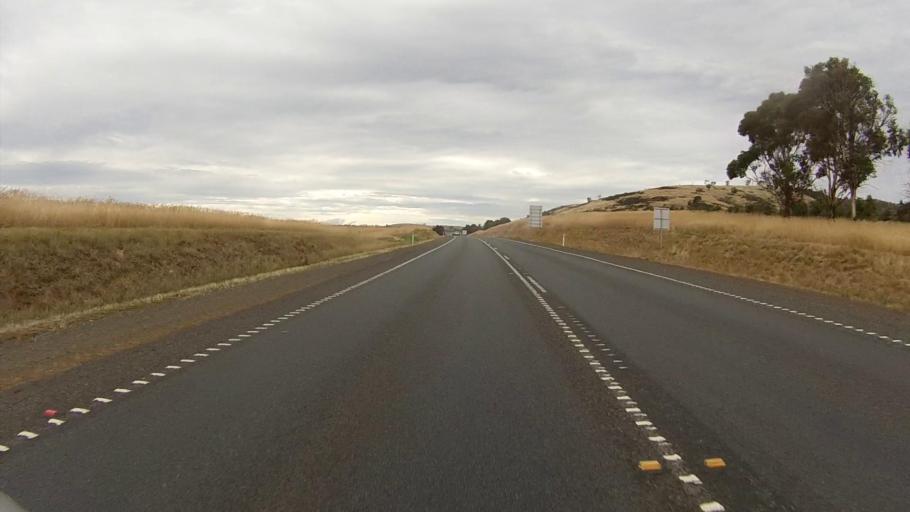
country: AU
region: Tasmania
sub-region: Brighton
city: Bridgewater
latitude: -42.3827
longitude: 147.3170
